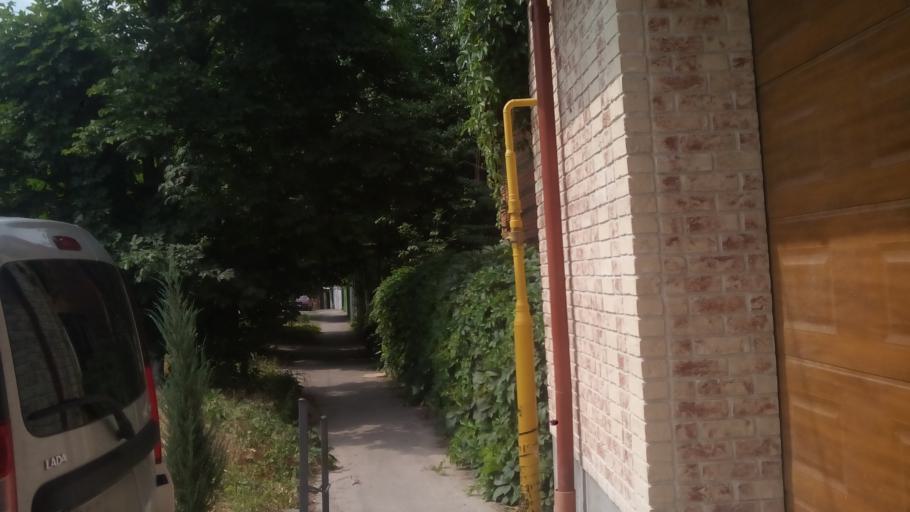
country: RU
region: Rostov
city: Rostov-na-Donu
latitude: 47.2152
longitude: 39.6712
